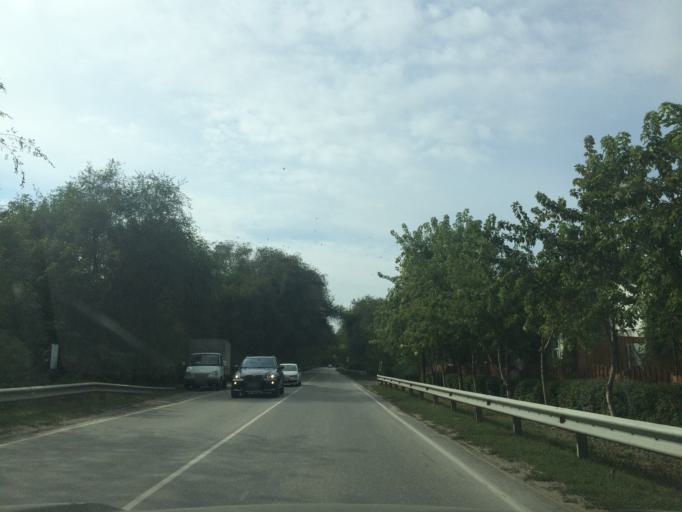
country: RU
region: Rostov
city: Kalinin
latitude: 47.1819
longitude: 39.6016
